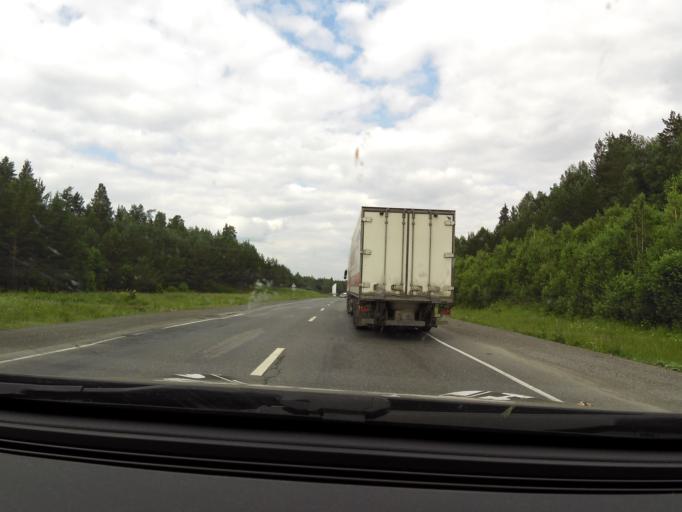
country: RU
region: Sverdlovsk
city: Druzhinino
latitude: 56.8185
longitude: 59.5653
